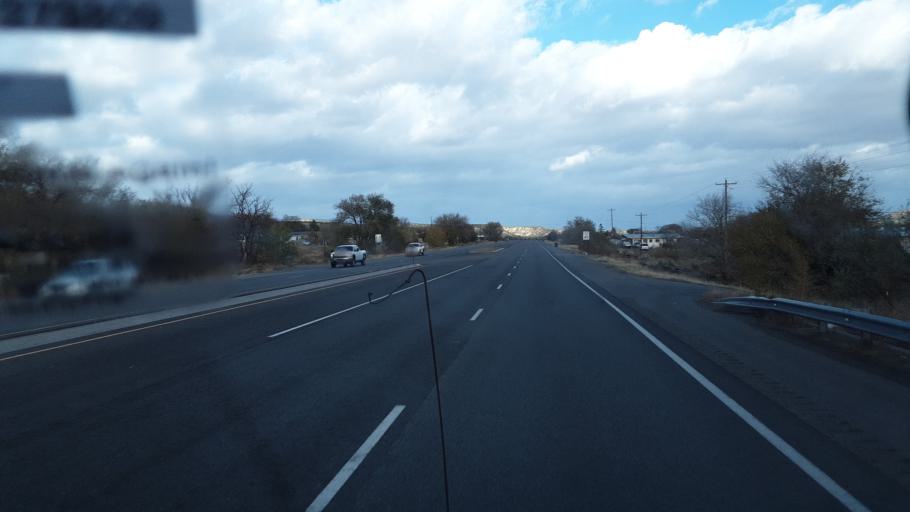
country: US
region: New Mexico
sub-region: Rio Arriba County
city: Ohkay Owingeh
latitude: 36.0407
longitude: -106.1009
